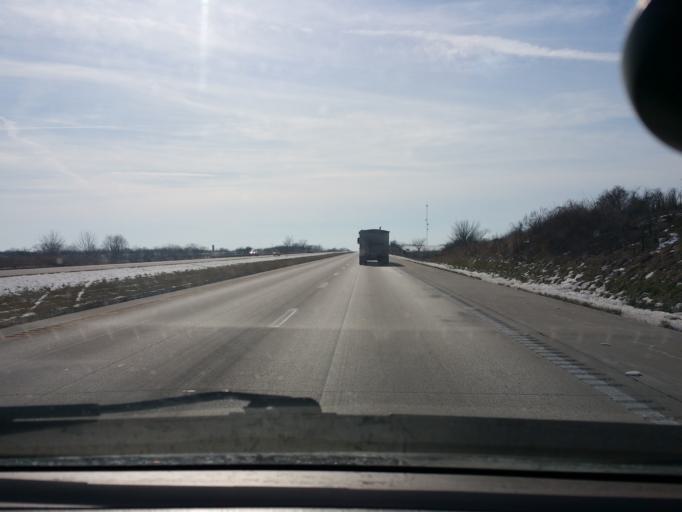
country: US
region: Missouri
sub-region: Clinton County
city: Lathrop
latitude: 39.6237
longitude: -94.2470
